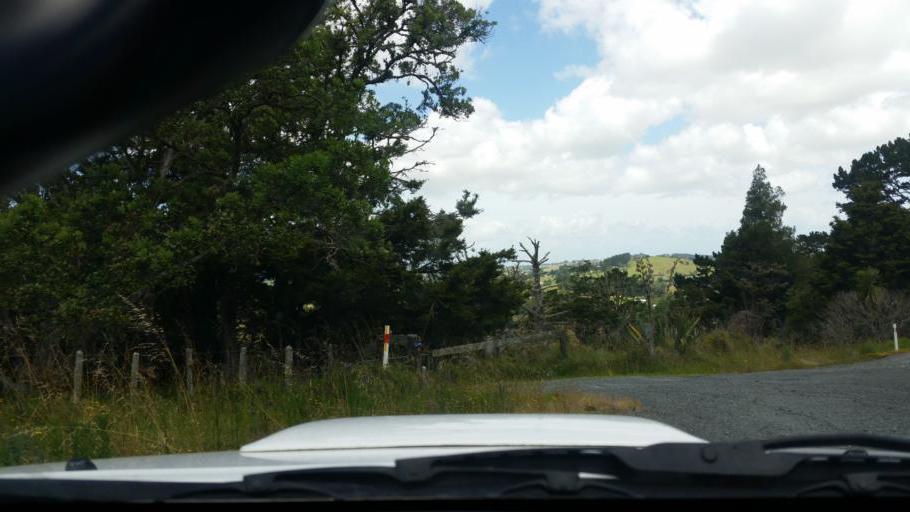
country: NZ
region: Northland
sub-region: Whangarei
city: Ruakaka
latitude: -36.0855
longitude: 174.2406
